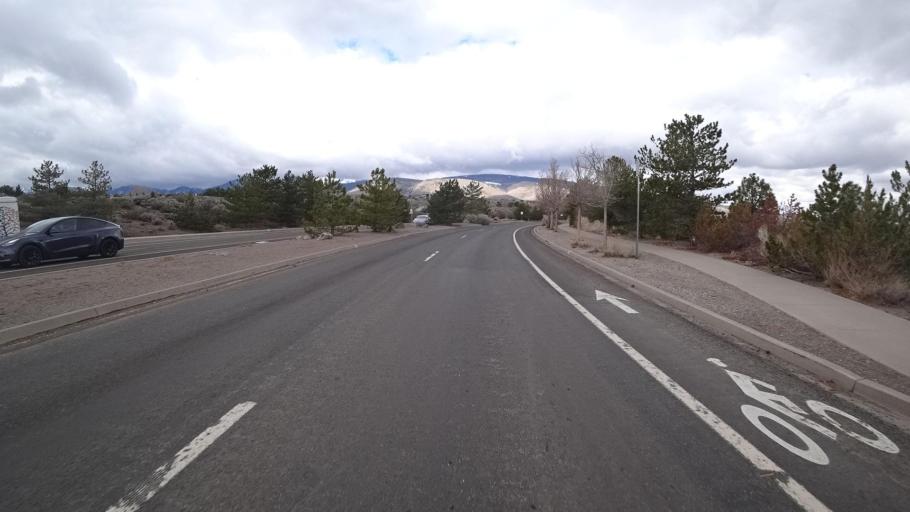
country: US
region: Nevada
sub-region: Washoe County
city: Reno
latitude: 39.4047
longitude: -119.7997
